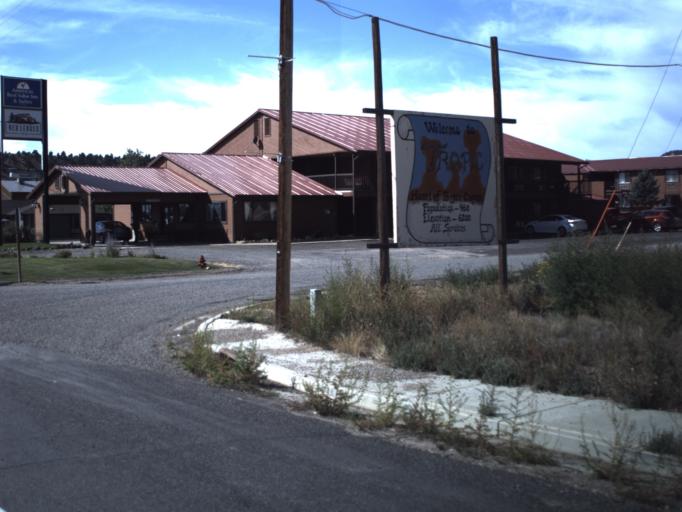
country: US
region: Utah
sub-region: Garfield County
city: Panguitch
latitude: 37.6272
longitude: -112.0819
